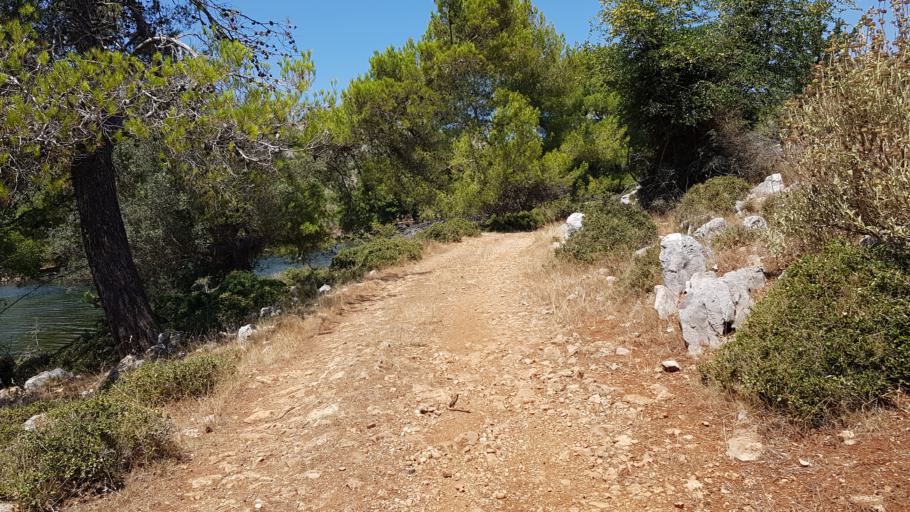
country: AL
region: Vlore
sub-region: Rrethi i Sarandes
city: Xarre
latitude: 39.7547
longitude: 19.9963
